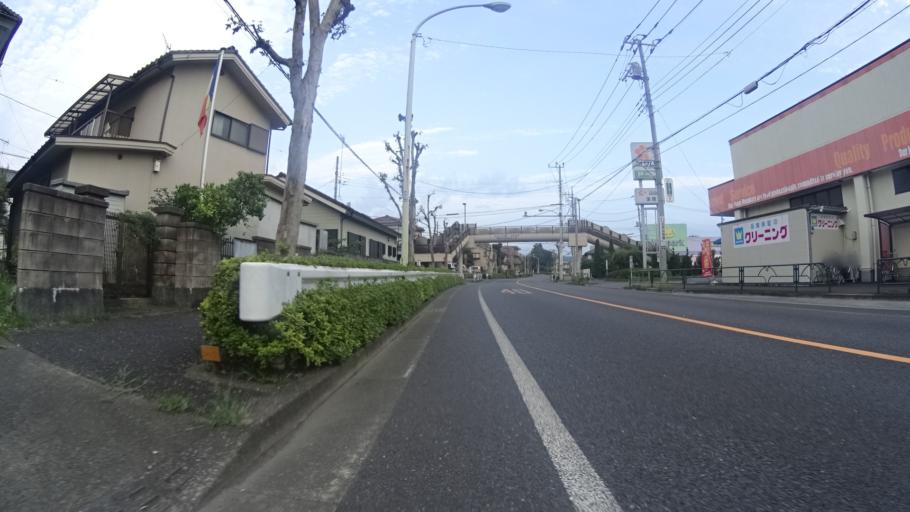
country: JP
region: Tokyo
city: Ome
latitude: 35.7731
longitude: 139.2844
